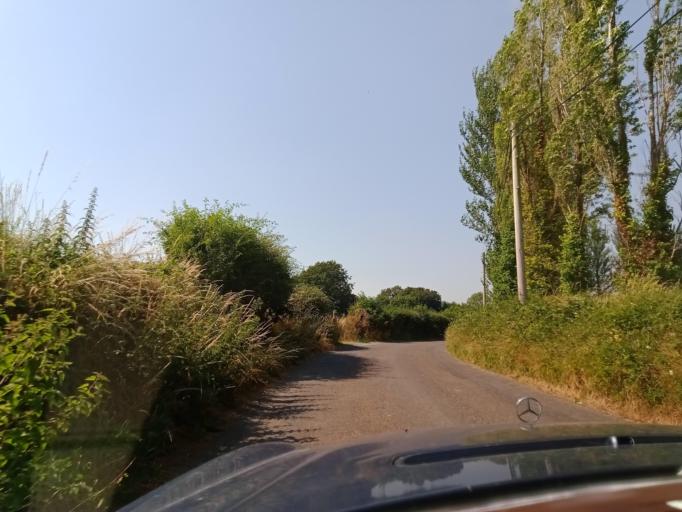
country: IE
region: Leinster
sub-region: Kilkenny
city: Piltown
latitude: 52.3343
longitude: -7.3023
